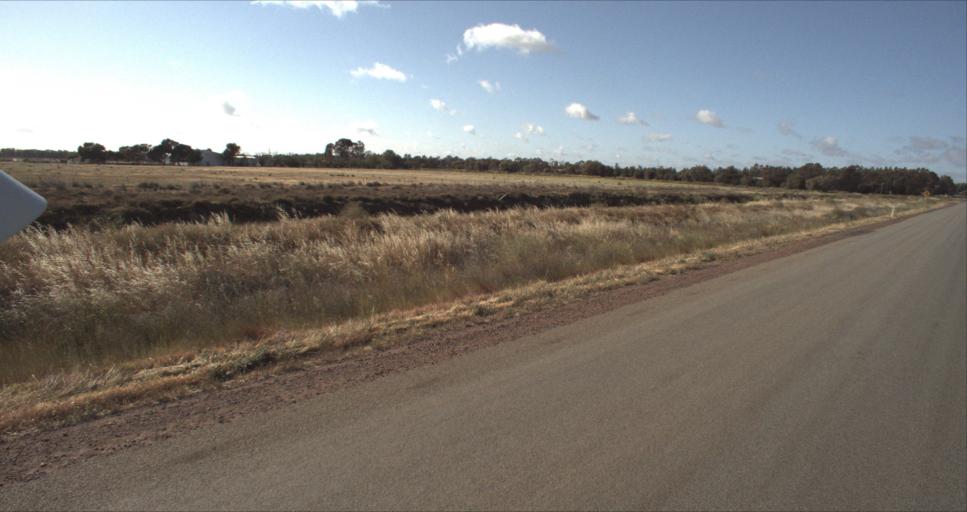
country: AU
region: New South Wales
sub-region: Leeton
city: Leeton
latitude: -34.5243
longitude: 146.3900
